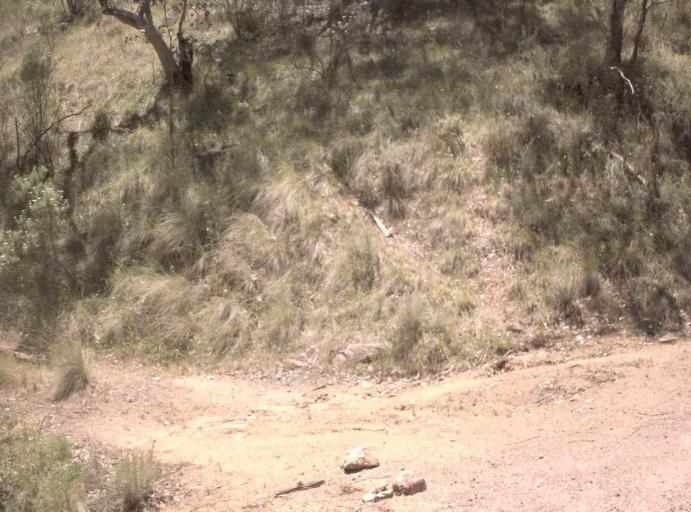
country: AU
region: New South Wales
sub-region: Snowy River
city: Jindabyne
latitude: -36.9310
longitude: 148.3552
